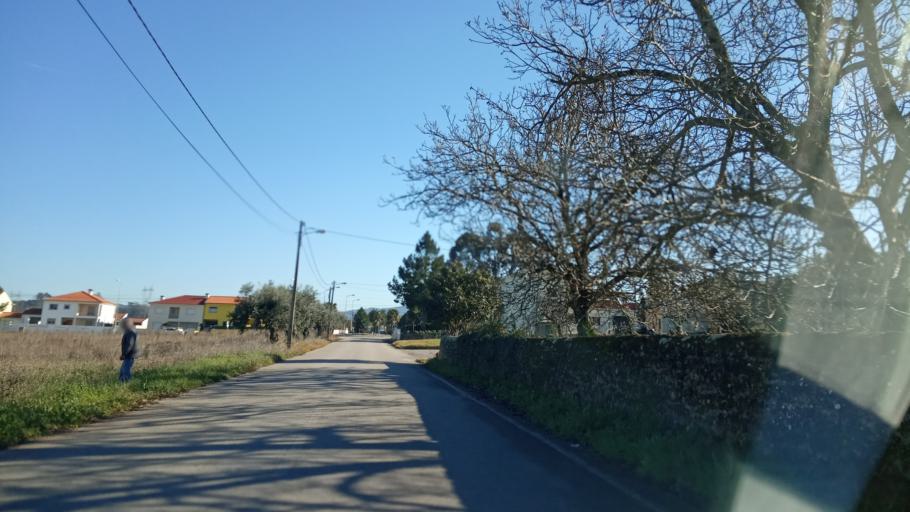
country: PT
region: Aveiro
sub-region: Anadia
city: Anadia
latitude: 40.4264
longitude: -8.4269
